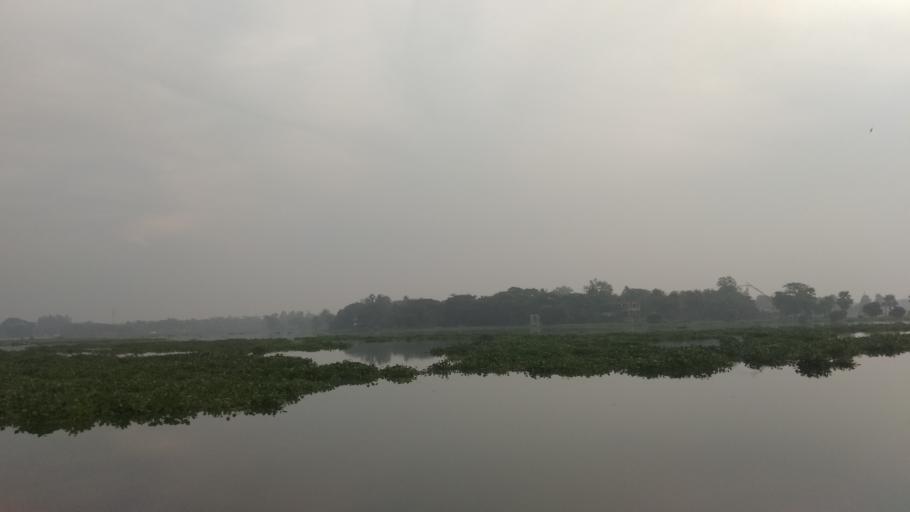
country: BD
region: Dhaka
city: Tungi
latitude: 23.8510
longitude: 90.4473
